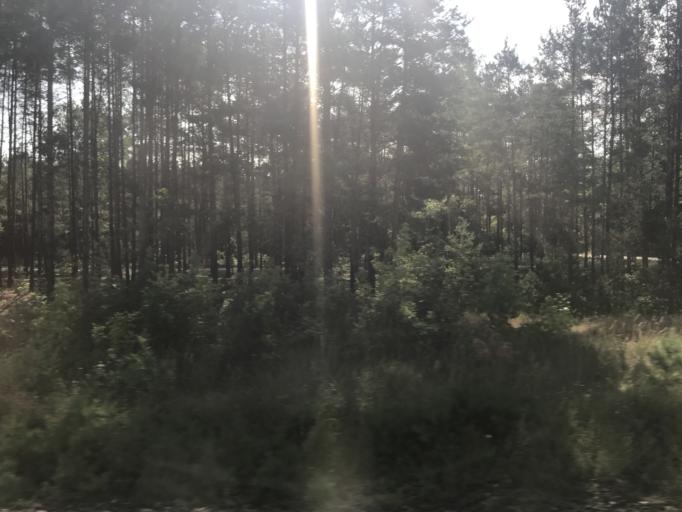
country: PL
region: Kujawsko-Pomorskie
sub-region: Powiat bydgoski
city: Osielsko
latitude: 53.2205
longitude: 18.0338
